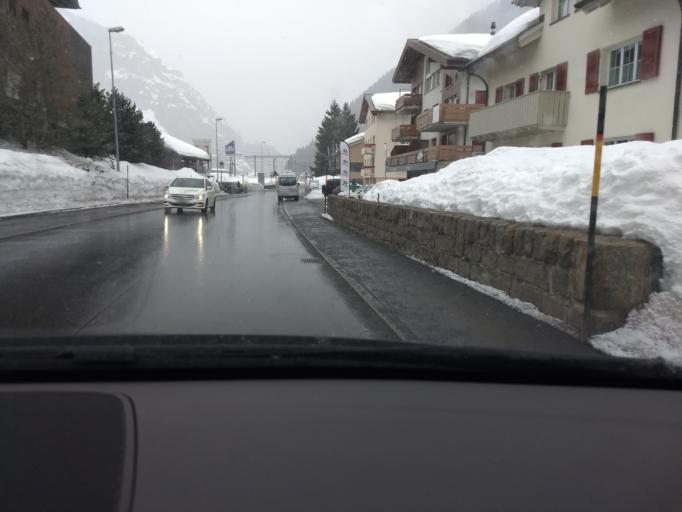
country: CH
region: Uri
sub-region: Uri
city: Andermatt
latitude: 46.6364
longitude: 8.5953
